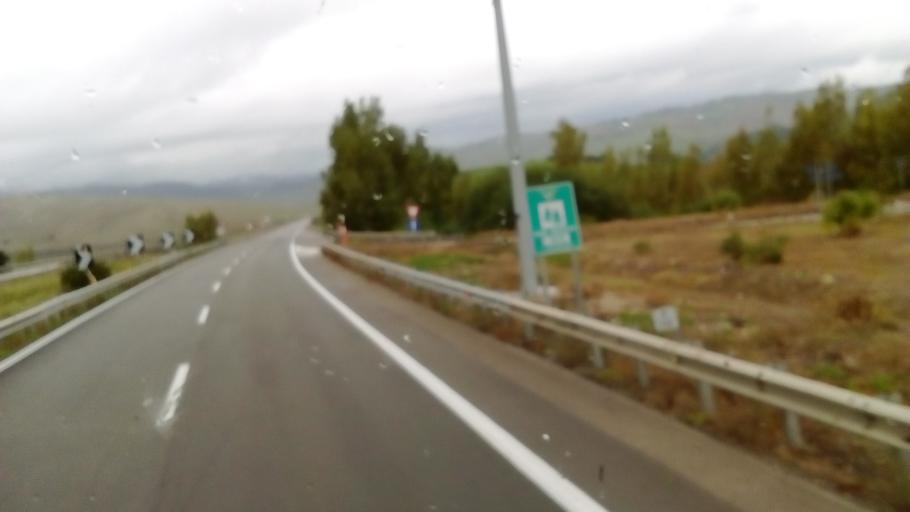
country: IT
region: Sicily
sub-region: Enna
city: Calascibetta
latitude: 37.5679
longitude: 14.2280
